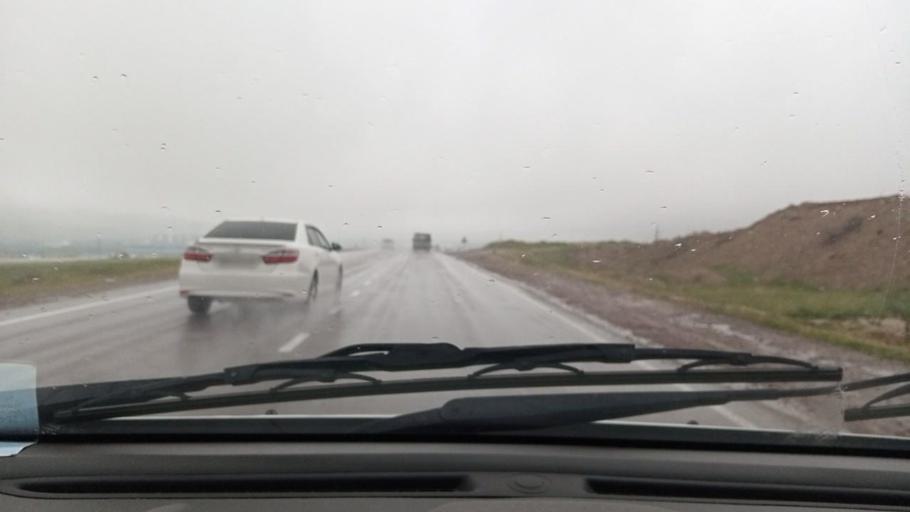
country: UZ
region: Toshkent
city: Angren
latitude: 41.0411
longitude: 70.1476
